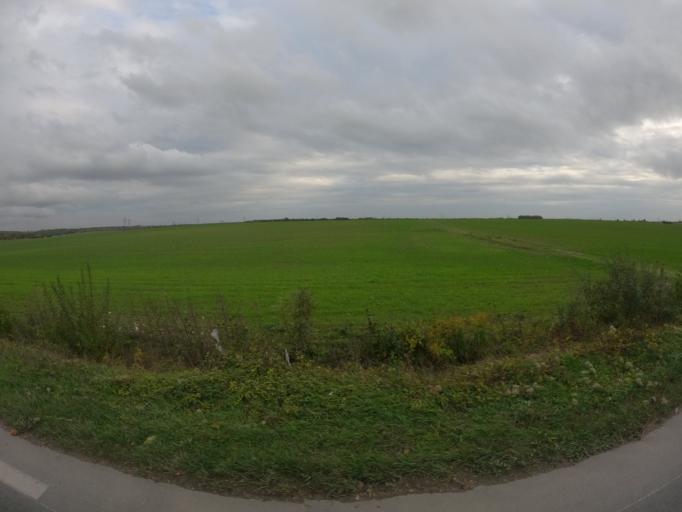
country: FR
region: Ile-de-France
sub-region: Departement de Seine-et-Marne
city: Le Pin
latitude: 48.9060
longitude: 2.6193
